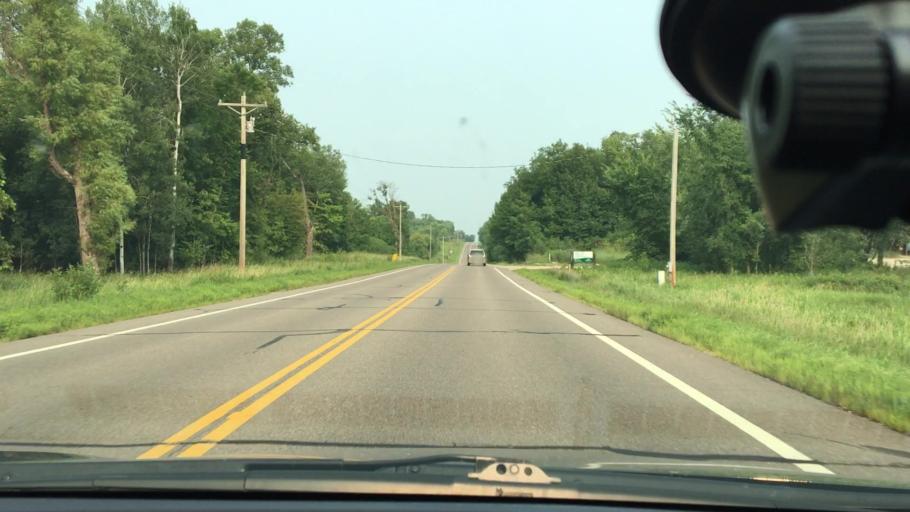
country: US
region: Minnesota
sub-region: Hennepin County
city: Champlin
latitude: 45.1882
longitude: -93.4523
